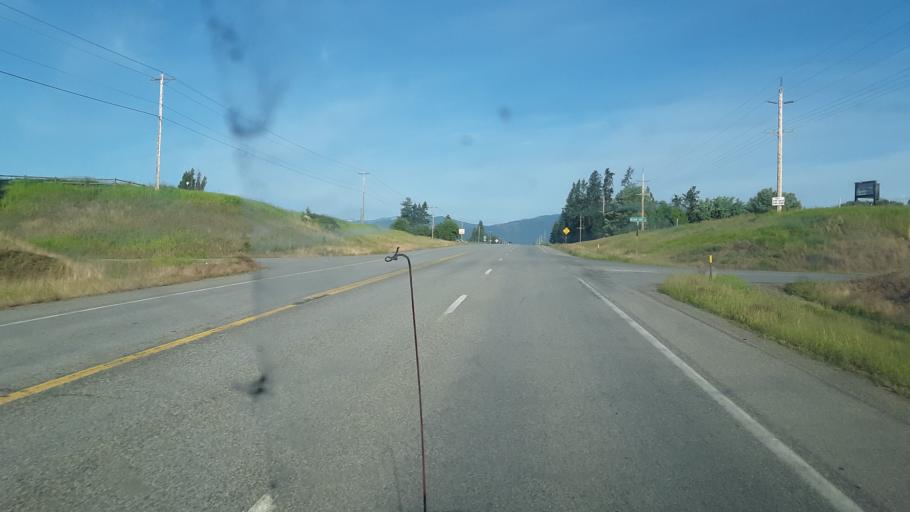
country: US
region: Idaho
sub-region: Boundary County
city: Bonners Ferry
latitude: 48.7317
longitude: -116.2556
